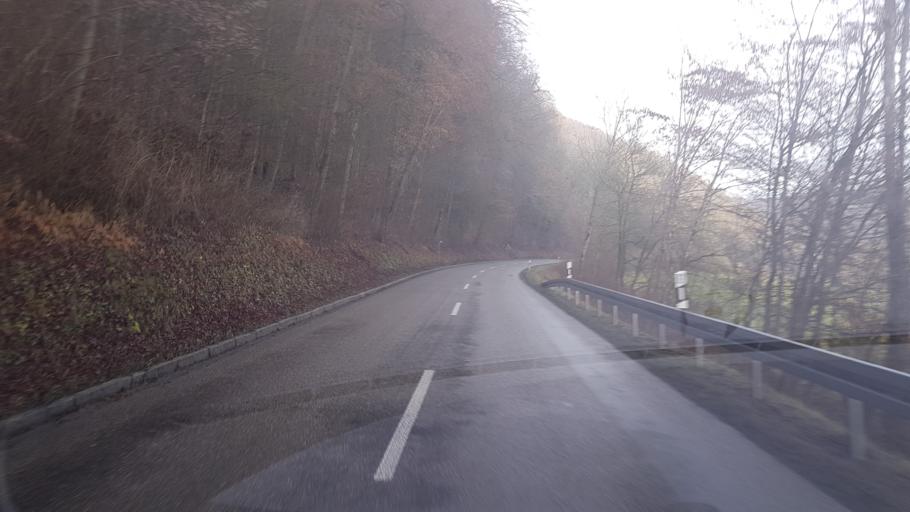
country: DE
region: Baden-Wuerttemberg
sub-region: Regierungsbezirk Stuttgart
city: Ilshofen
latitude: 49.2258
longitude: 9.9081
